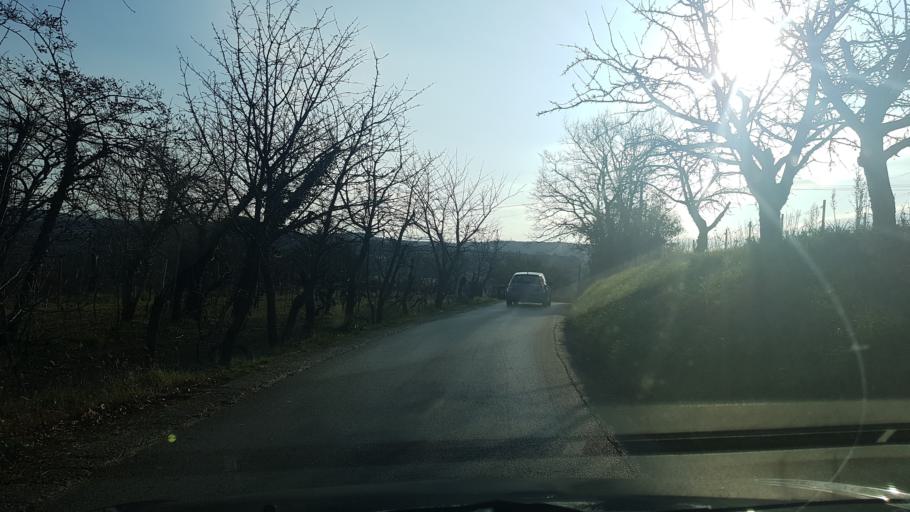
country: SI
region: Koper-Capodistria
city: Prade
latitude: 45.5351
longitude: 13.7764
